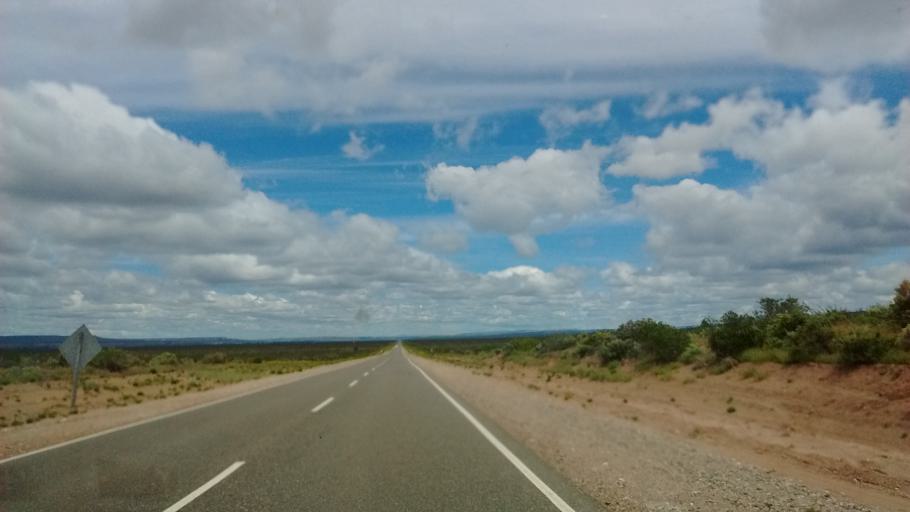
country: AR
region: Neuquen
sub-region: Departamento de Picun Leufu
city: Picun Leufu
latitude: -39.7865
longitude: -69.6651
